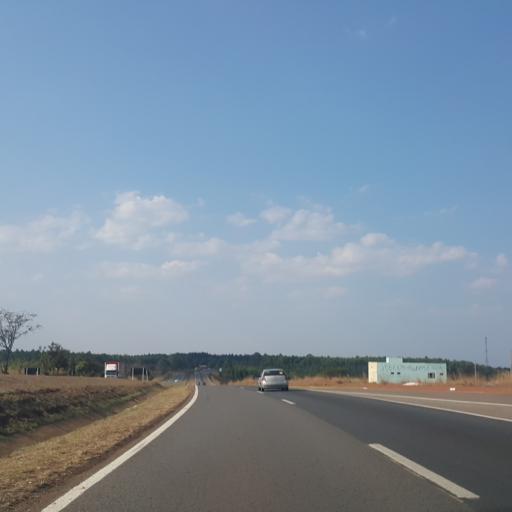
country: BR
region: Goias
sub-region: Abadiania
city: Abadiania
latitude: -16.1903
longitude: -48.7025
